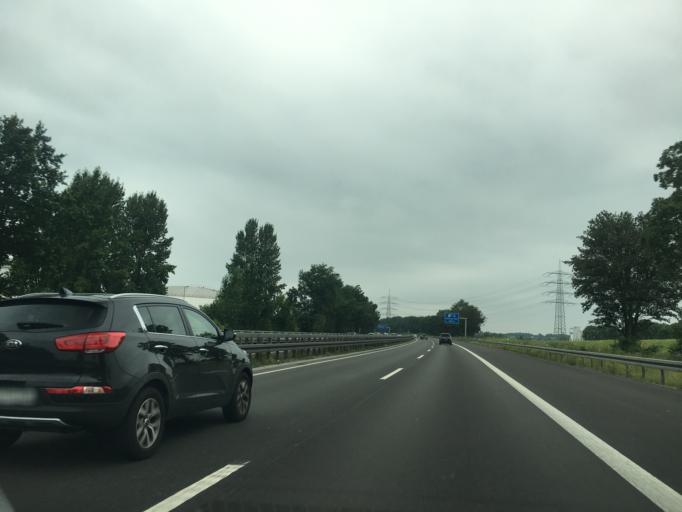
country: DE
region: North Rhine-Westphalia
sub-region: Regierungsbezirk Munster
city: Bottrop
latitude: 51.5080
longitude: 6.9592
